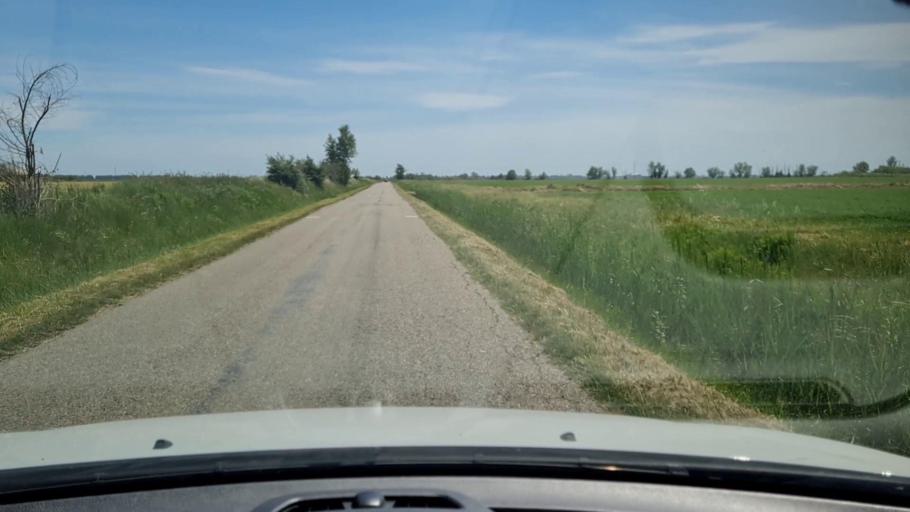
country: FR
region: Languedoc-Roussillon
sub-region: Departement du Gard
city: Saint-Gilles
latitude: 43.6152
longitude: 4.4259
